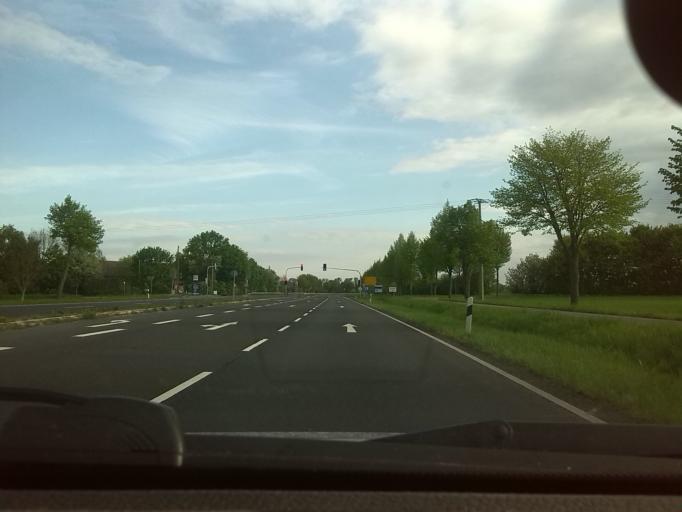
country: DE
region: Hesse
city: Lampertheim
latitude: 49.5802
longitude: 8.4478
